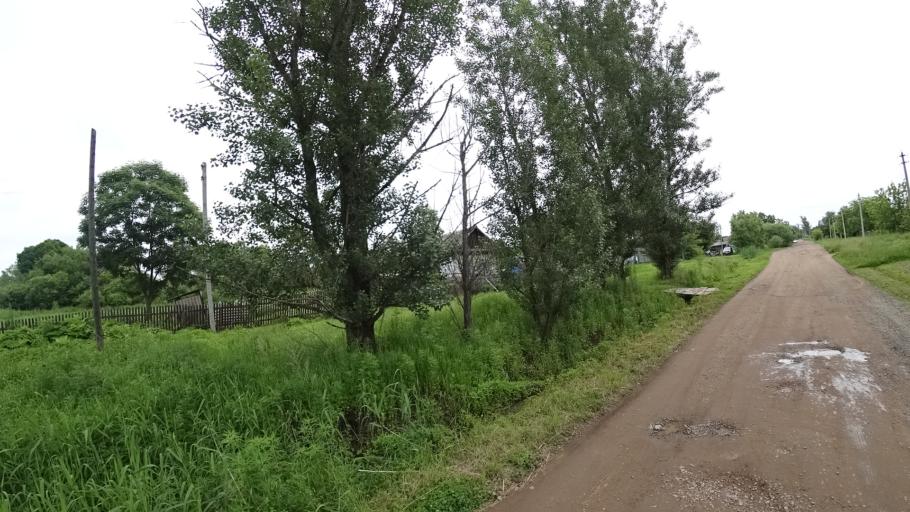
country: RU
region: Primorskiy
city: Novosysoyevka
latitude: 44.2512
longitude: 133.3758
